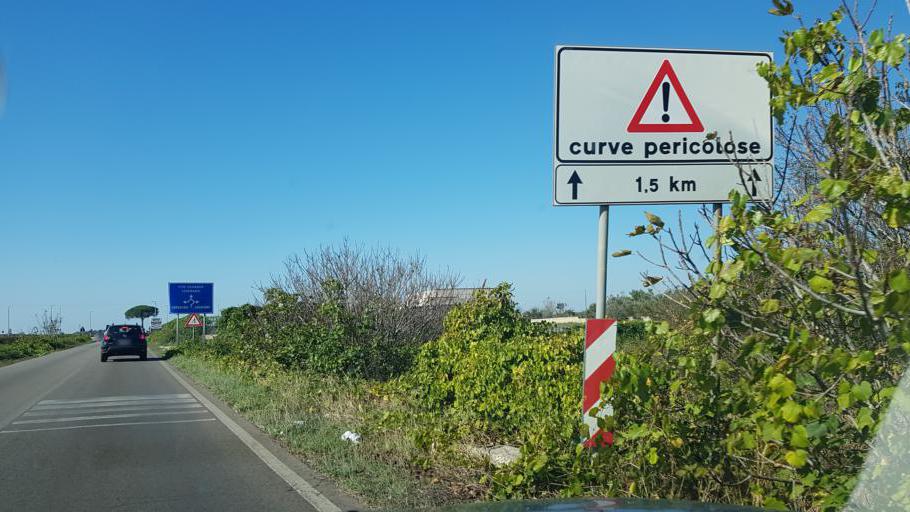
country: IT
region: Apulia
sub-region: Provincia di Lecce
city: Magliano
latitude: 40.3153
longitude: 18.0464
